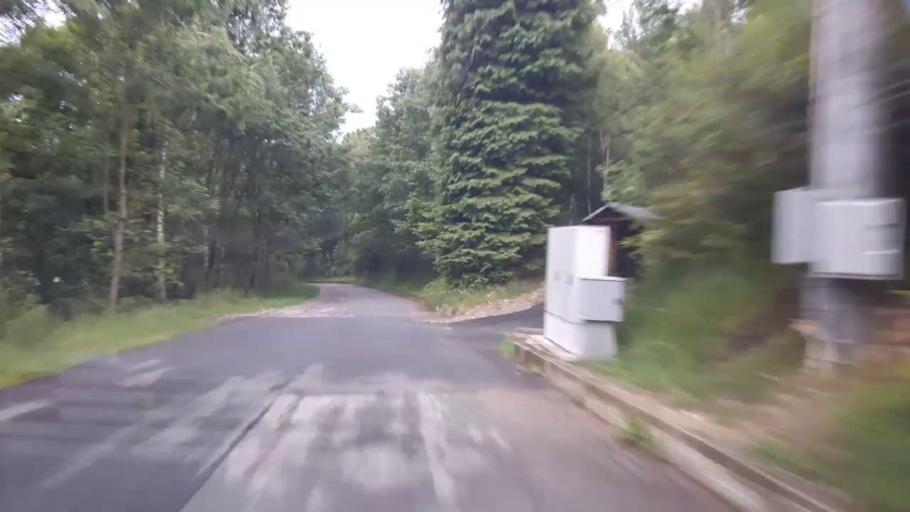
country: IT
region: Piedmont
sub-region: Provincia Verbano-Cusio-Ossola
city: Gignese
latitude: 45.8682
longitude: 8.4982
